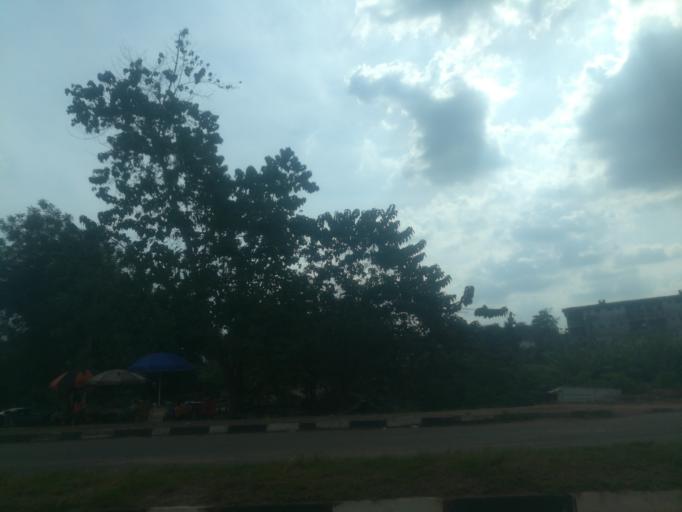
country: NG
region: Ogun
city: Abeokuta
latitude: 7.1362
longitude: 3.3456
